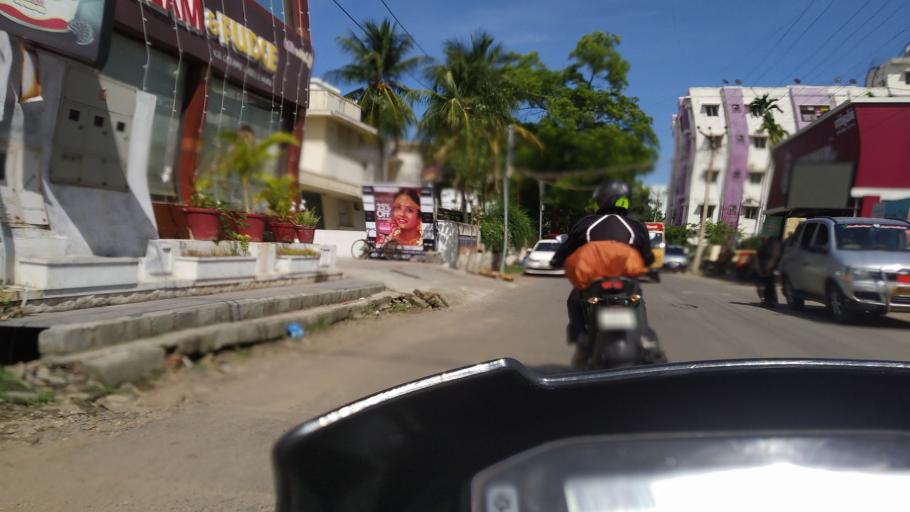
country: IN
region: Tamil Nadu
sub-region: Salem
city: Salem
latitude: 11.6764
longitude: 78.1425
